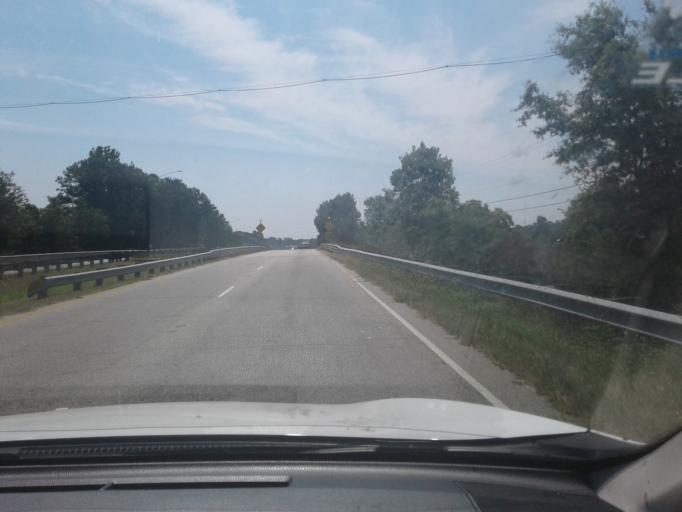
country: US
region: North Carolina
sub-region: Harnett County
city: Erwin
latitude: 35.3299
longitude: -78.6635
